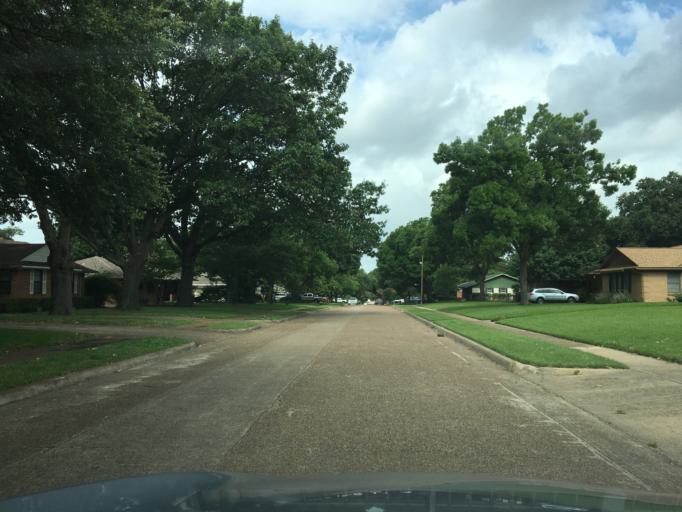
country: US
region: Texas
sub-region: Dallas County
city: Richardson
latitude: 32.9389
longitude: -96.7200
